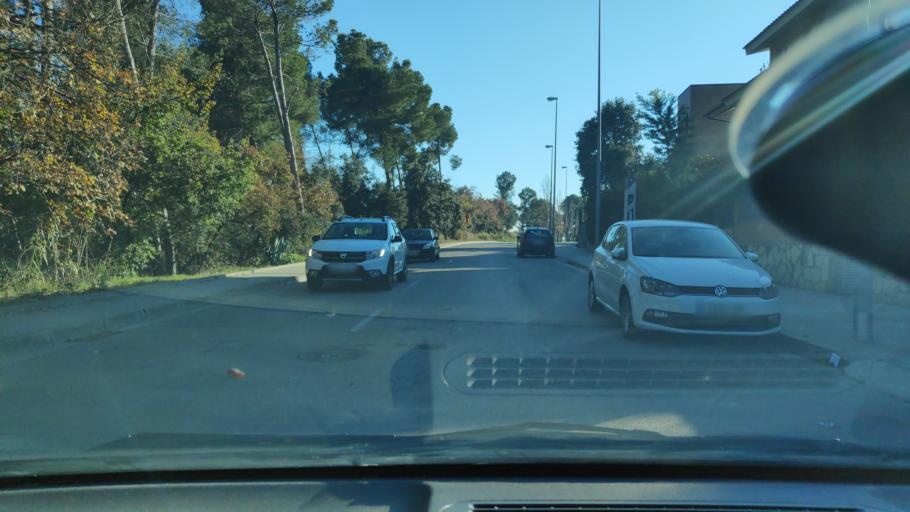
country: ES
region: Catalonia
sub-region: Provincia de Barcelona
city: Sant Quirze del Valles
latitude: 41.5589
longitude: 2.0769
